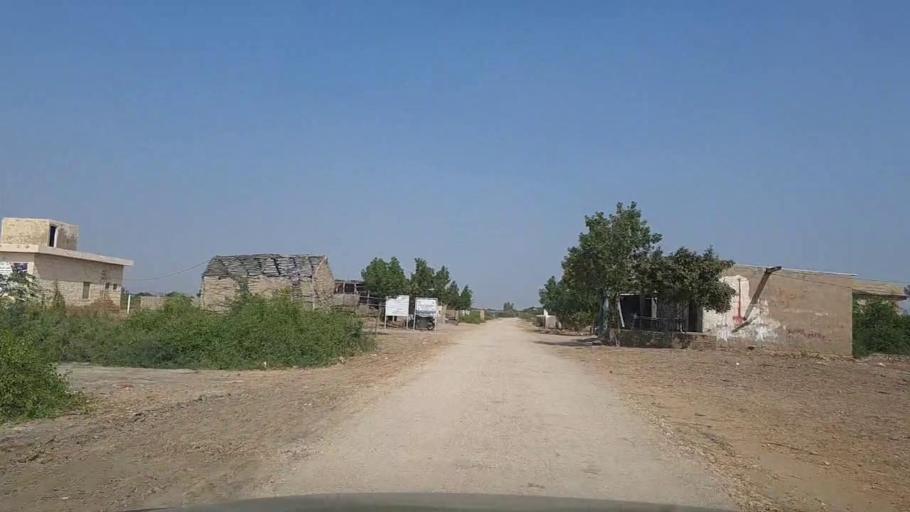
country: PK
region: Sindh
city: Thatta
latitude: 24.6138
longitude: 67.9579
